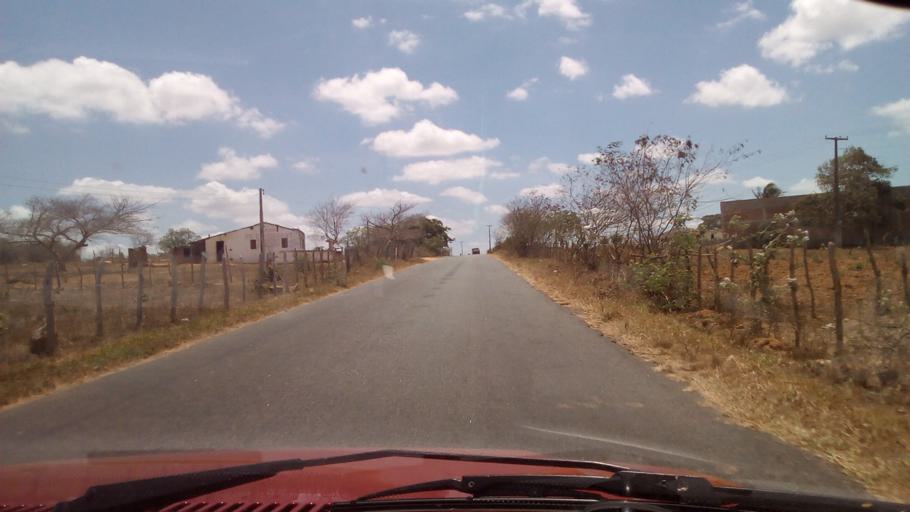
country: BR
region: Paraiba
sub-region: Cacimba De Dentro
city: Cacimba de Dentro
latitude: -6.6203
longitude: -35.7996
